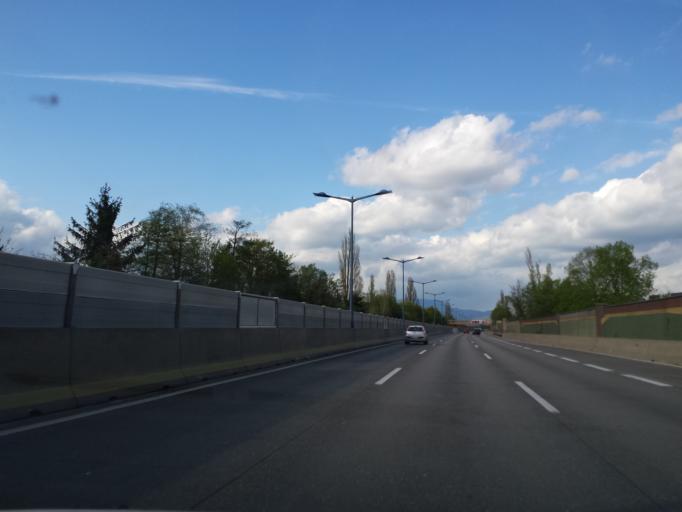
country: AT
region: Styria
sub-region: Politischer Bezirk Graz-Umgebung
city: Seiersberg
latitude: 47.0195
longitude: 15.4094
